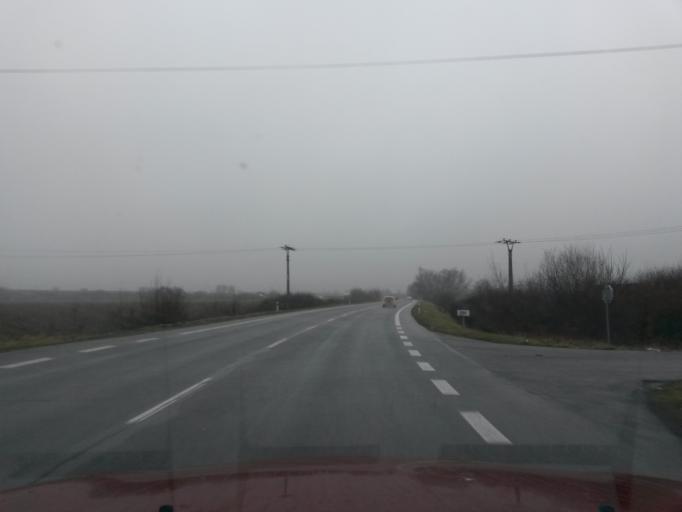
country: SK
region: Presovsky
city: Vranov nad Topl'ou
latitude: 48.8683
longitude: 21.7047
